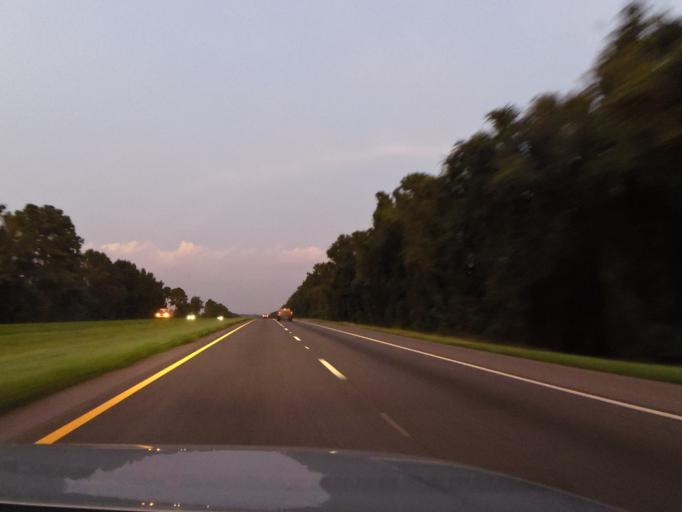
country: US
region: Florida
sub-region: Madison County
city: Madison
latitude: 30.4353
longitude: -83.4944
